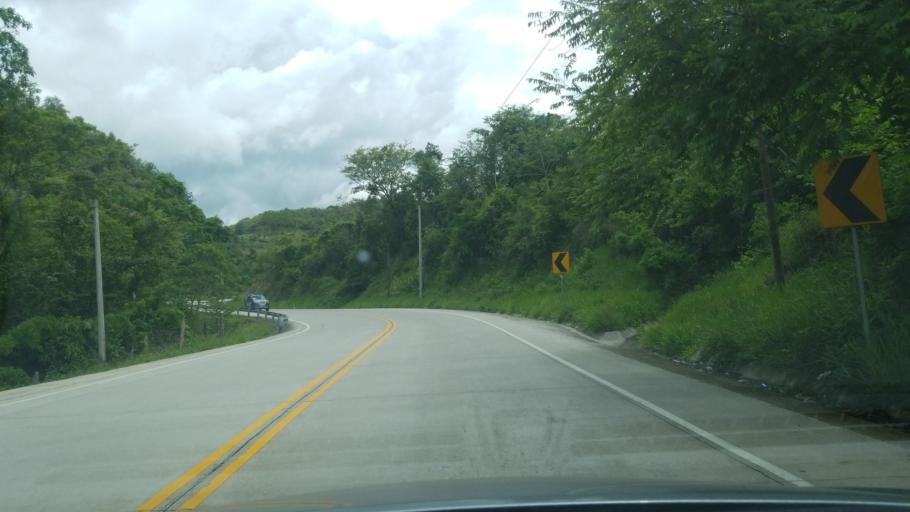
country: HN
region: Copan
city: Florida
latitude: 14.9988
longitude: -88.8413
